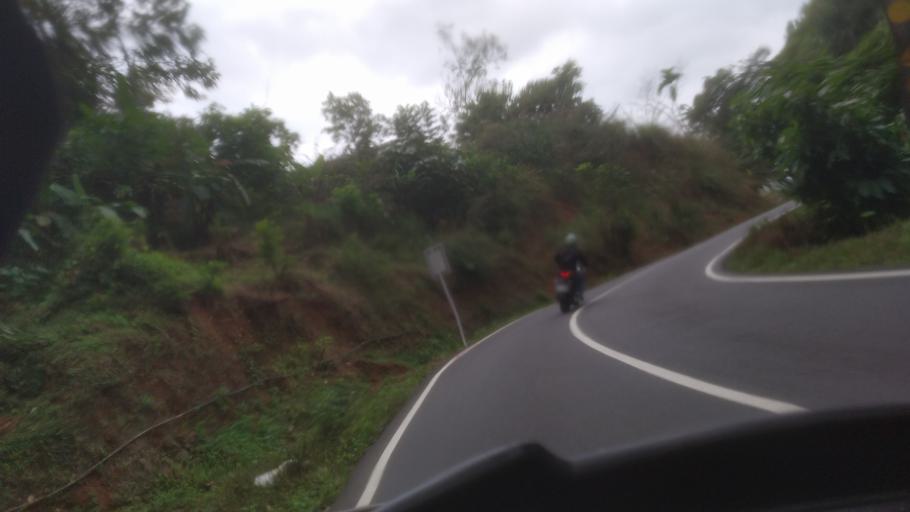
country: IN
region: Kerala
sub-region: Idukki
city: Idukki
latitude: 9.9643
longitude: 77.0010
